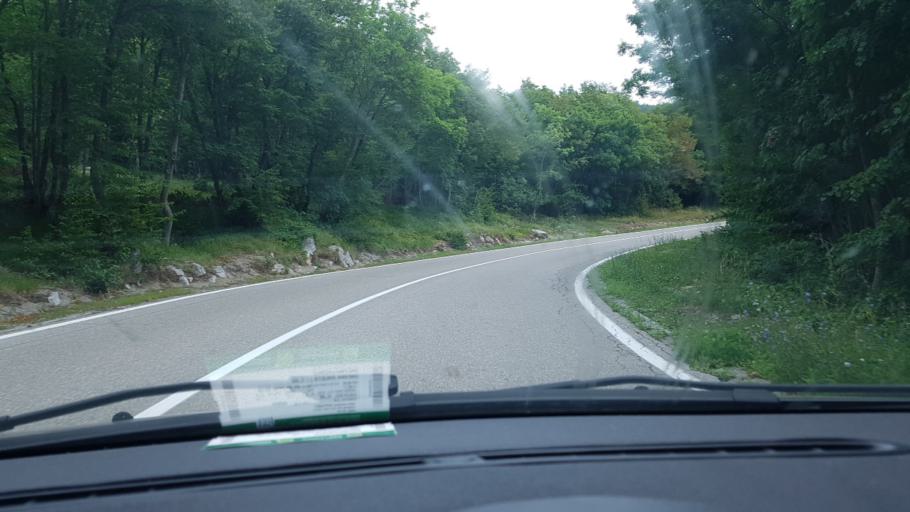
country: HR
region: Primorsko-Goranska
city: Hreljin
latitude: 45.3431
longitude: 14.6084
